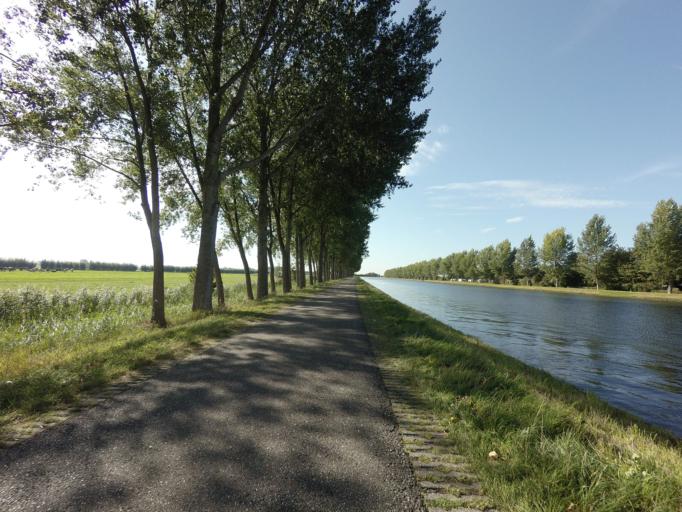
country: NL
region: Utrecht
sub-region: Gemeente Vianen
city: Vianen
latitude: 51.9454
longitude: 5.0485
